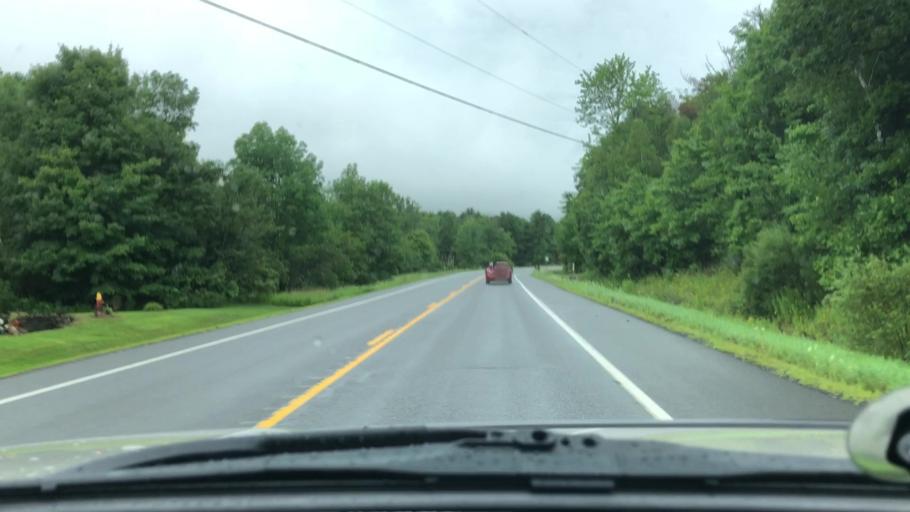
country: US
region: New York
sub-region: Greene County
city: Cairo
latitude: 42.3217
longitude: -74.1777
